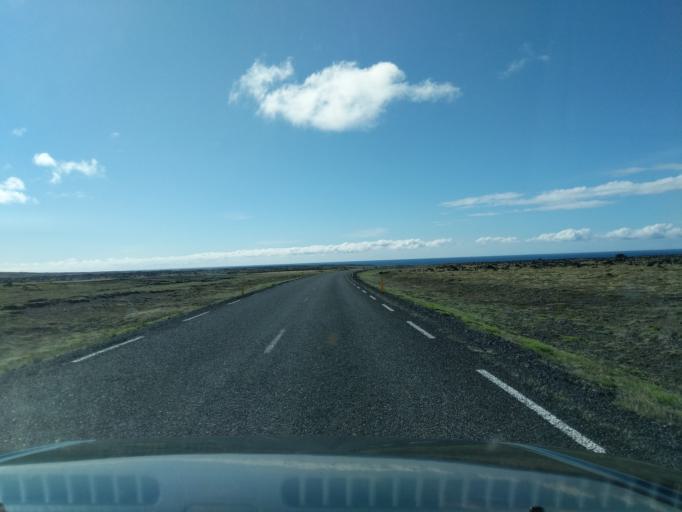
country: IS
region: West
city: Olafsvik
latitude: 64.8729
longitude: -23.9300
